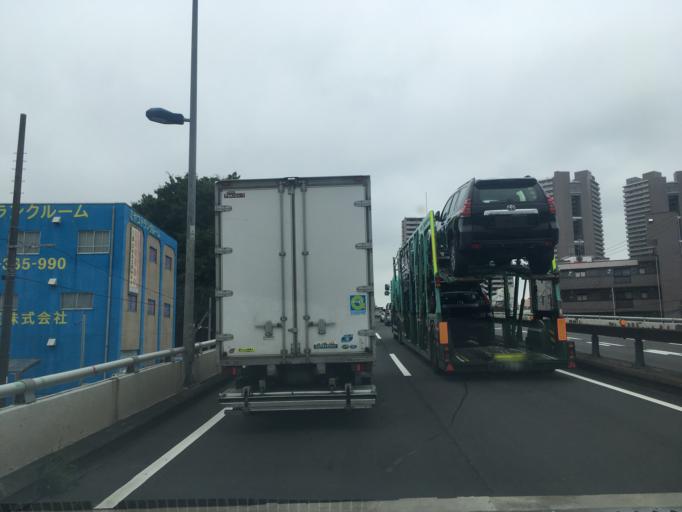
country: JP
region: Tokyo
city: Hachioji
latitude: 35.5995
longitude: 139.3389
